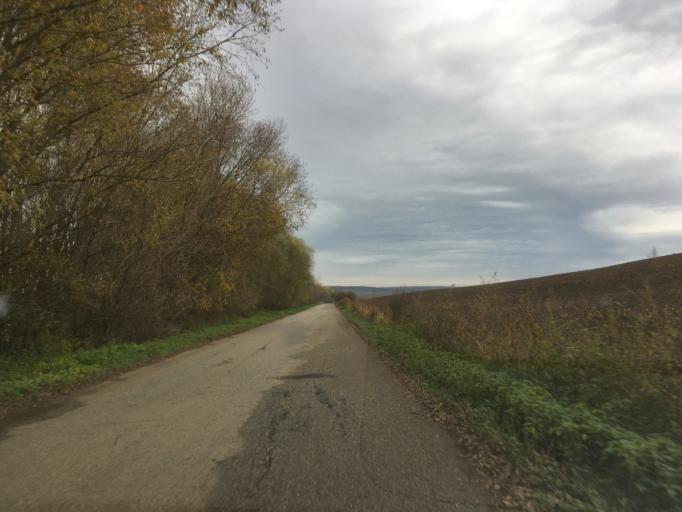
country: SK
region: Nitriansky
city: Svodin
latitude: 48.0426
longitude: 18.3715
